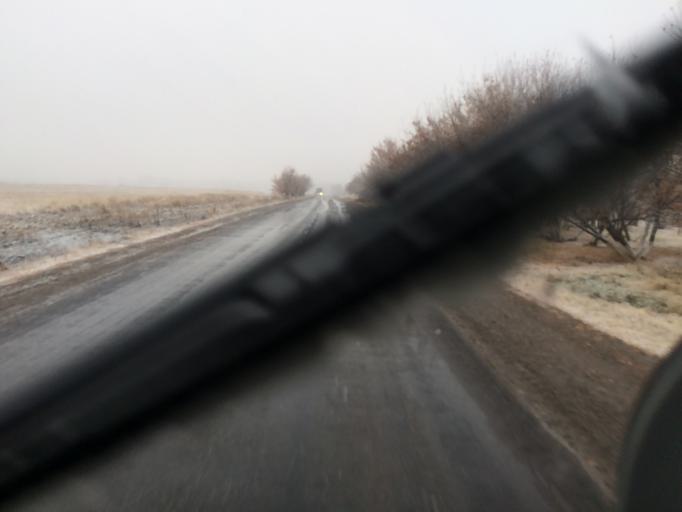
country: KG
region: Chuy
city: Ivanovka
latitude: 42.9654
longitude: 75.0080
